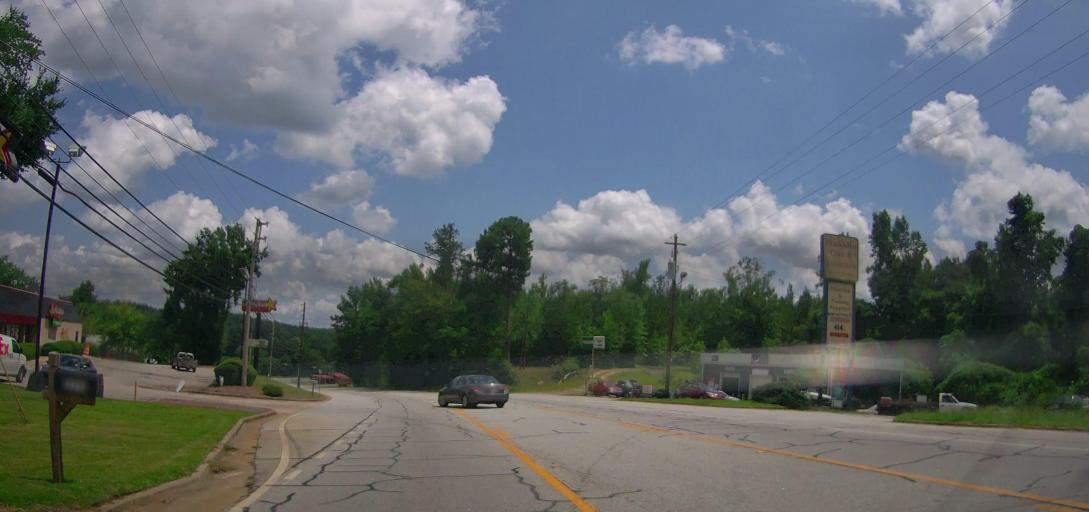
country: US
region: Georgia
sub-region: Heard County
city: Franklin
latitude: 33.2801
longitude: -85.1061
